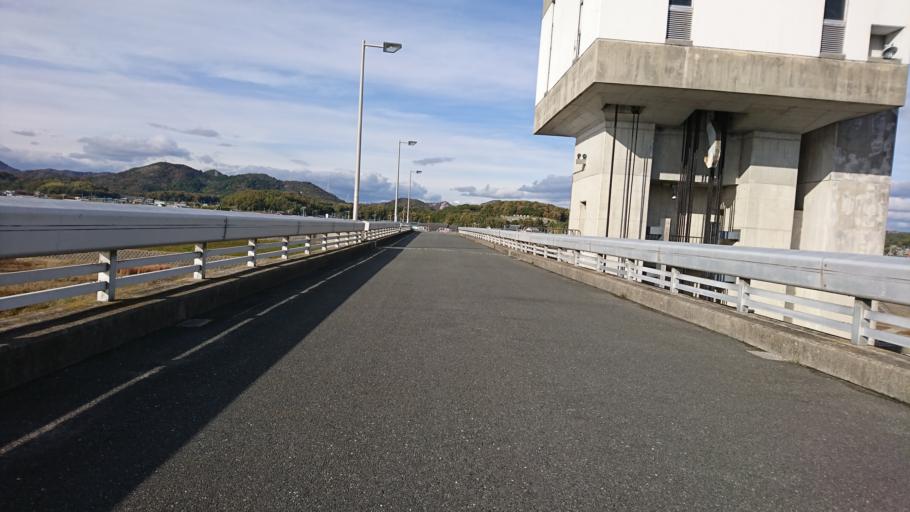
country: JP
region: Hyogo
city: Kakogawacho-honmachi
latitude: 34.7959
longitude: 134.8908
